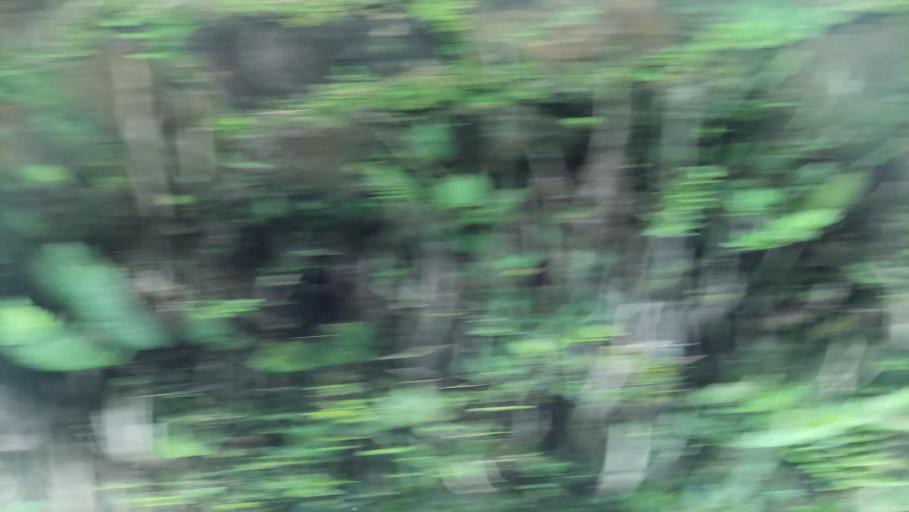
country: TW
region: Taipei
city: Taipei
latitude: 25.1444
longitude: 121.6075
